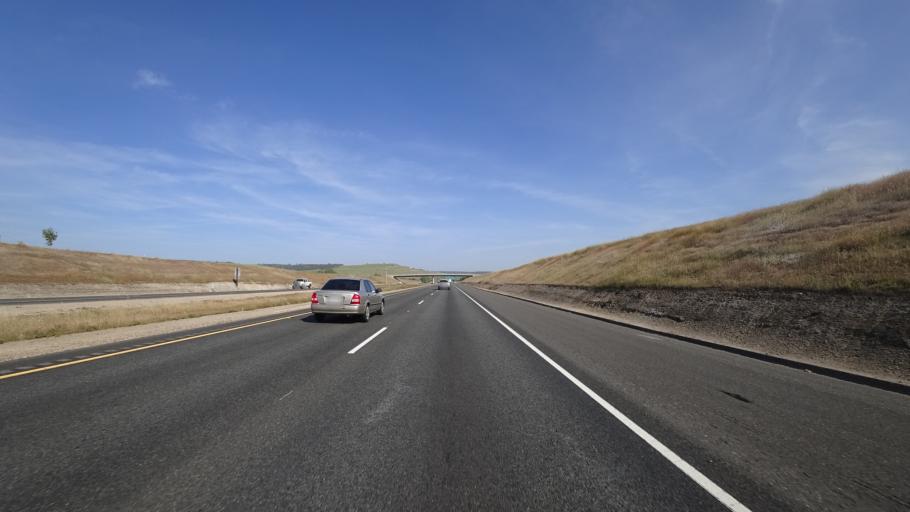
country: US
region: California
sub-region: Butte County
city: Thermalito
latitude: 39.5897
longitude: -121.6373
